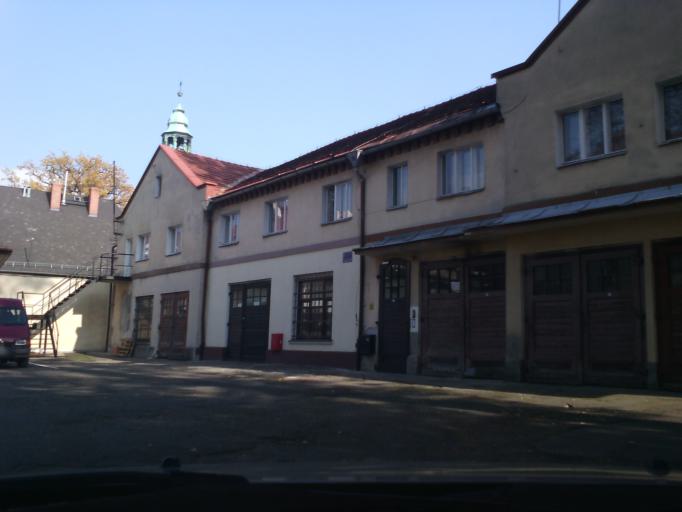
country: PL
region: Lower Silesian Voivodeship
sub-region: Jelenia Gora
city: Cieplice Slaskie Zdroj
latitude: 50.8646
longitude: 15.6832
